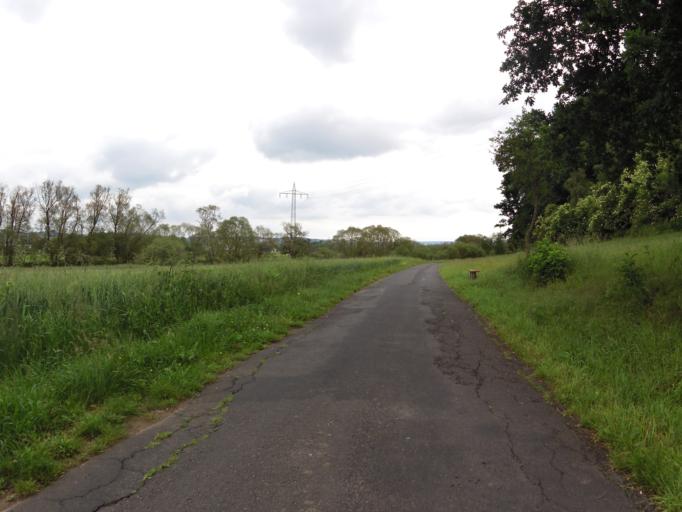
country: DE
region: Hesse
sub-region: Regierungsbezirk Kassel
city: Rotenburg an der Fulda
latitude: 50.9820
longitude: 9.7591
